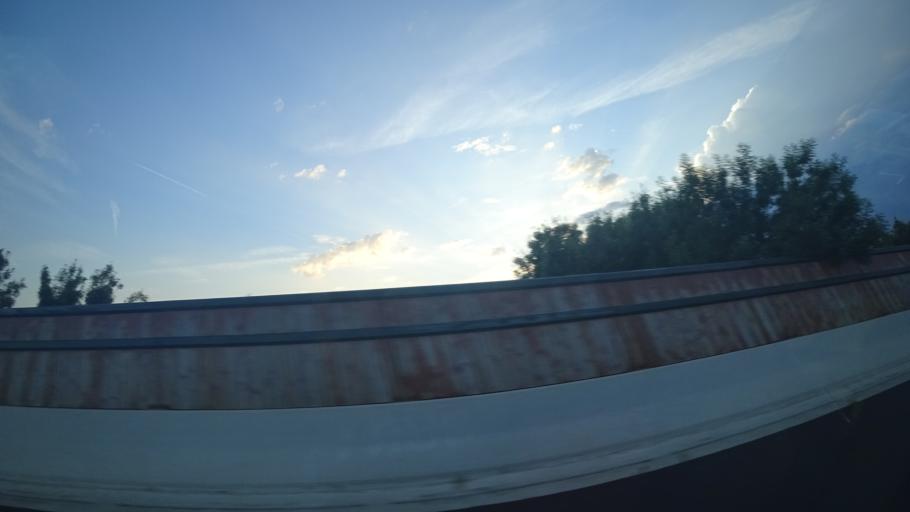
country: FR
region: Languedoc-Roussillon
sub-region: Departement de l'Herault
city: Pezenas
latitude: 43.4596
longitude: 3.4318
